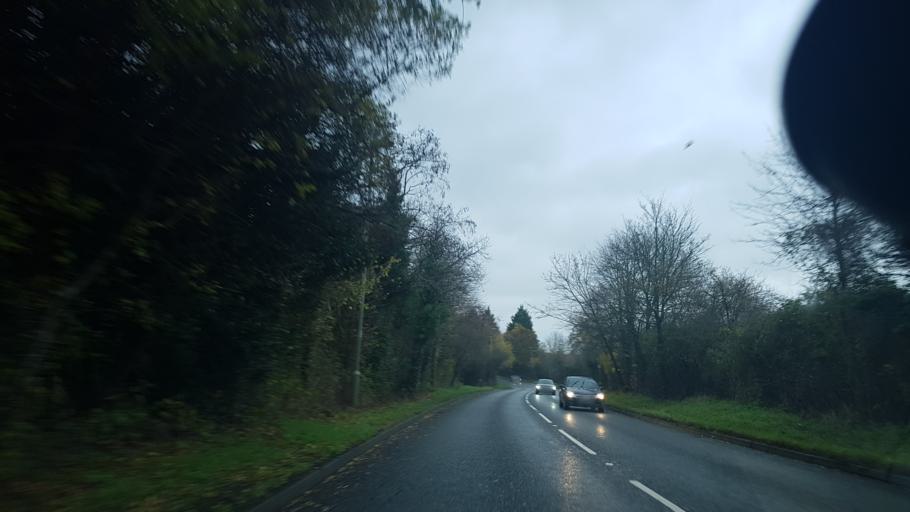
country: GB
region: England
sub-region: Surrey
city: Chilworth
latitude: 51.2498
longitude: -0.5262
